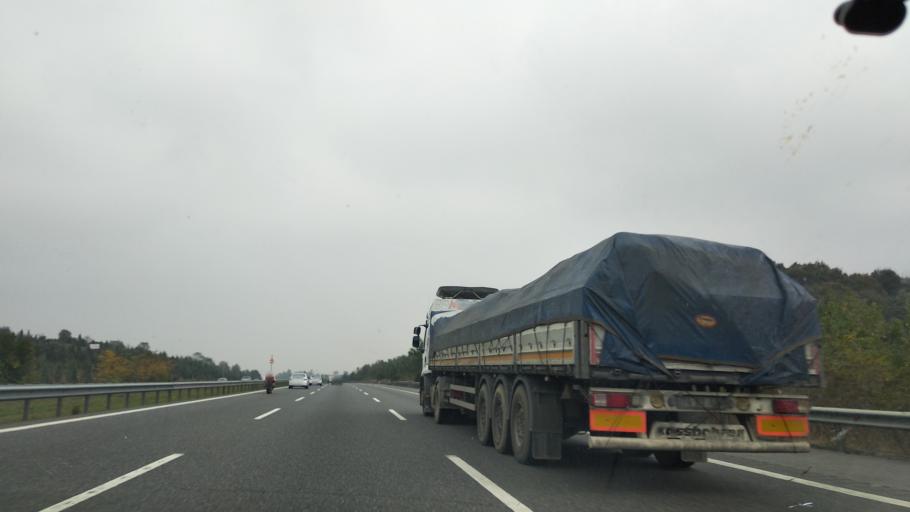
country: TR
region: Duzce
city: Gumusova
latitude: 40.8123
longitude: 30.9021
